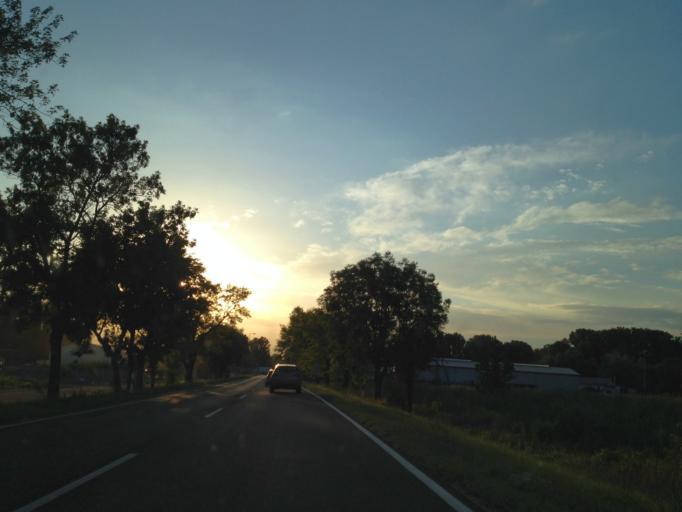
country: HU
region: Gyor-Moson-Sopron
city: Mosonmagyarovar
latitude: 47.8391
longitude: 17.2921
